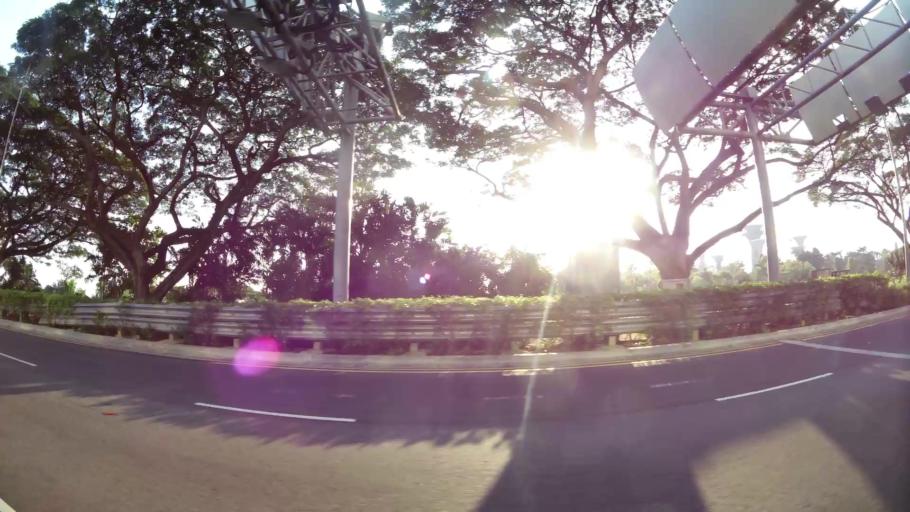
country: SG
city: Singapore
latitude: 1.2843
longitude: 103.8615
